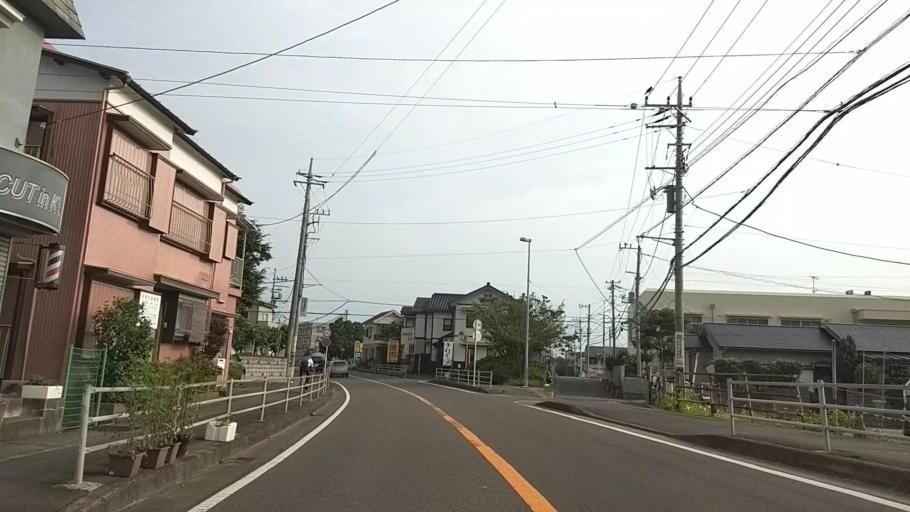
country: JP
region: Kanagawa
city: Oiso
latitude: 35.3375
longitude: 139.3100
